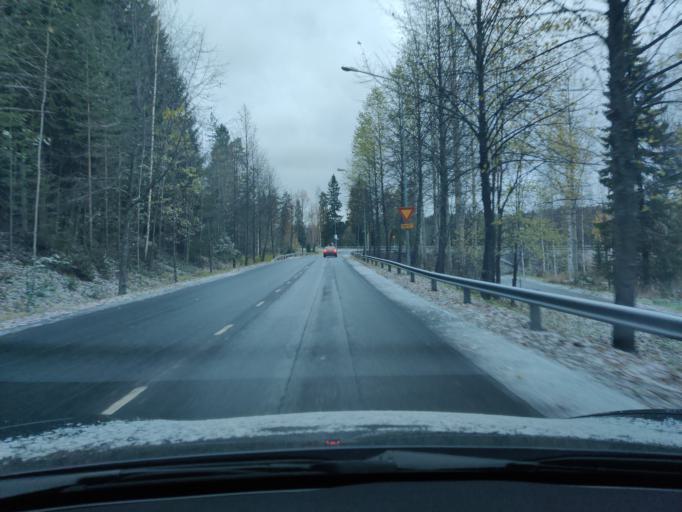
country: FI
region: Northern Savo
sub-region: Kuopio
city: Kuopio
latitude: 62.8410
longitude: 27.6344
